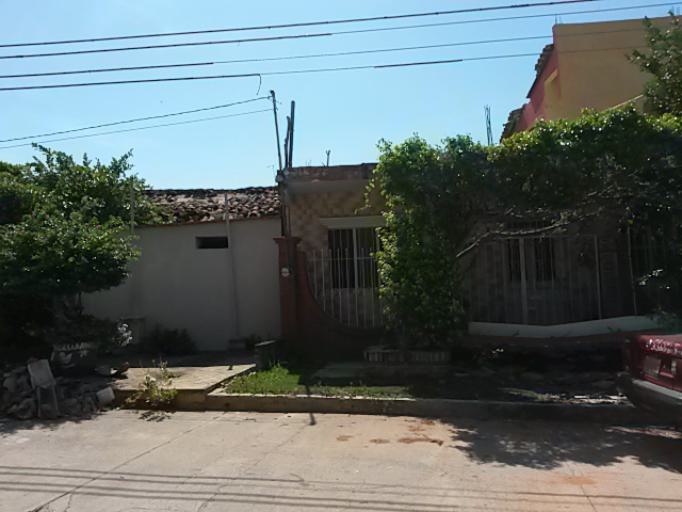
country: MX
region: Oaxaca
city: Asuncion Ixtaltepec
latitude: 16.5051
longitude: -95.0563
